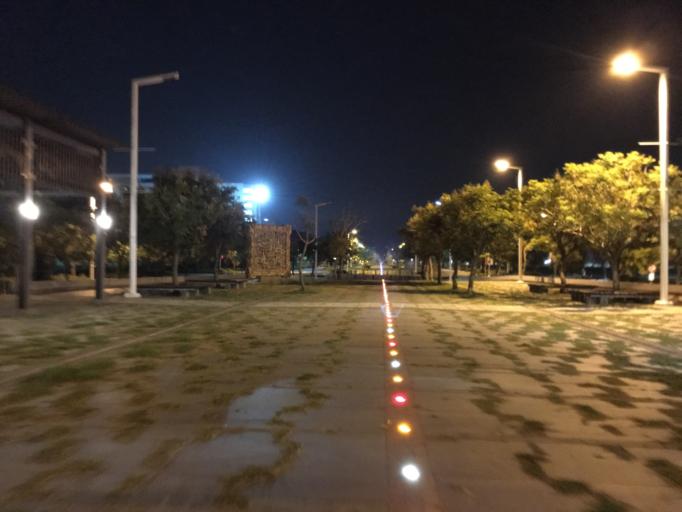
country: TW
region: Taiwan
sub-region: Chiayi
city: Taibao
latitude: 23.4621
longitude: 120.2928
